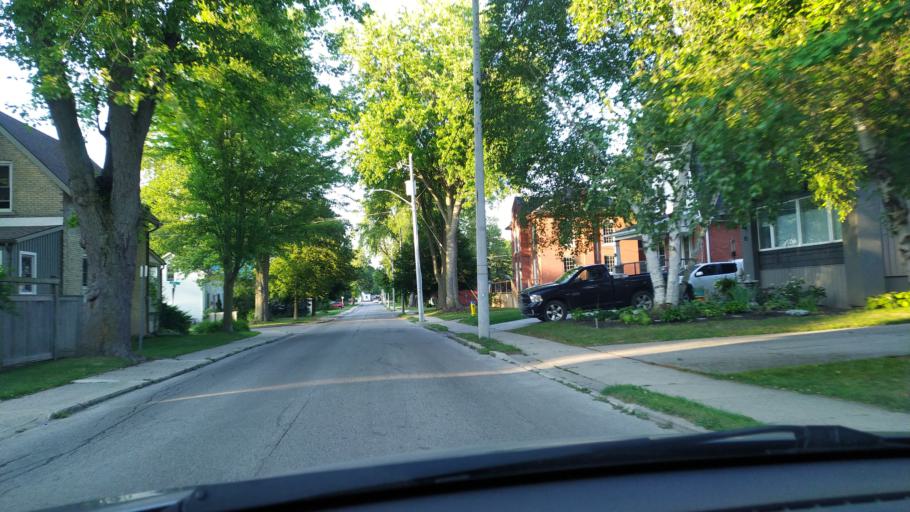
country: CA
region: Ontario
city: Stratford
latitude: 43.3609
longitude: -80.9857
